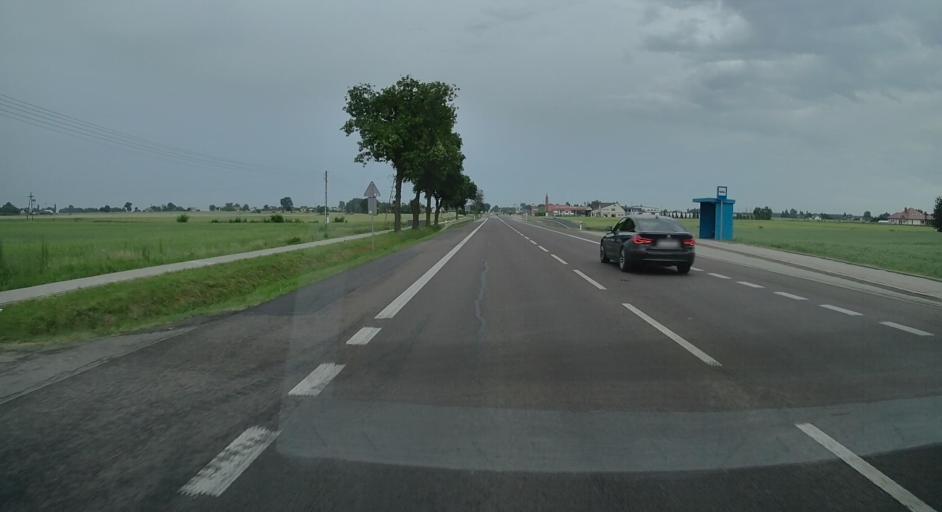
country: PL
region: Lublin Voivodeship
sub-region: Powiat bialski
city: Rzeczyca
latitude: 52.0259
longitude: 22.7140
